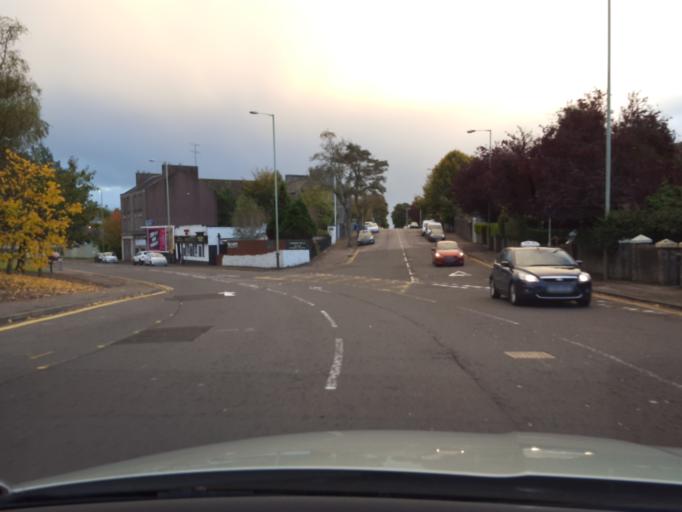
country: GB
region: Scotland
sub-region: Dundee City
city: Dundee
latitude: 56.4686
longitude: -3.0029
